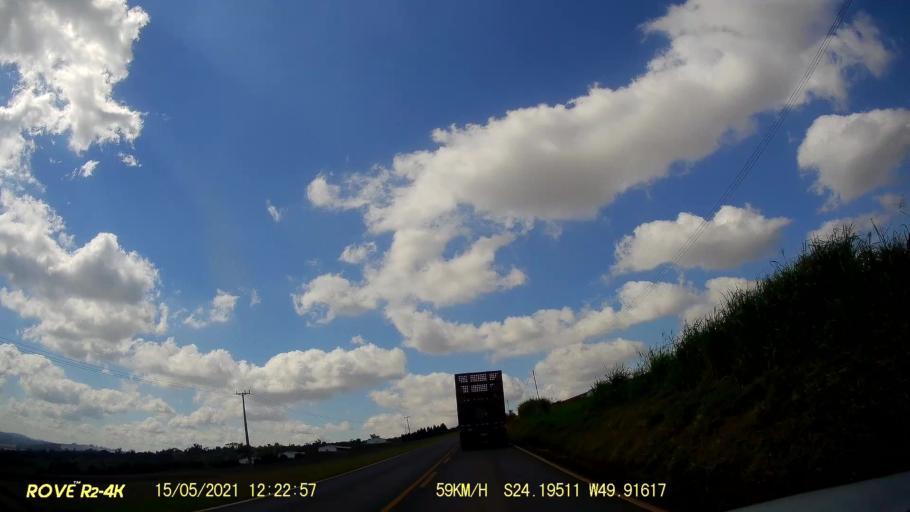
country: BR
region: Parana
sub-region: Jaguariaiva
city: Jaguariaiva
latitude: -24.1951
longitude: -49.9162
